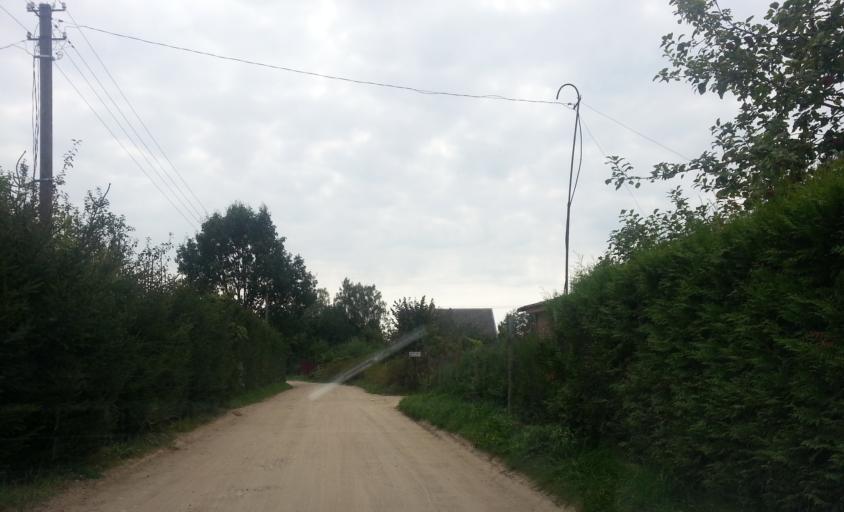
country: LT
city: Grigiskes
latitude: 54.7652
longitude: 25.0225
